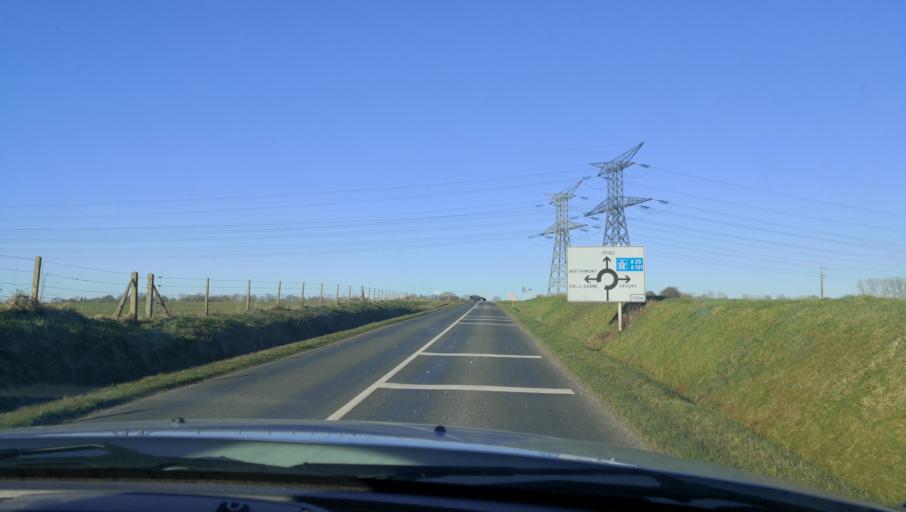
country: FR
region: Haute-Normandie
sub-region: Departement de la Seine-Maritime
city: Totes
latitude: 49.6551
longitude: 1.0198
